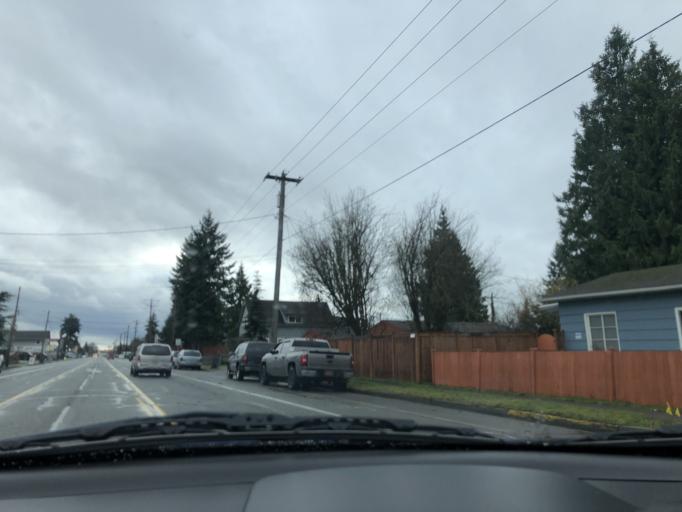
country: US
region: Washington
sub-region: Snohomish County
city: Marysville
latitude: 48.0573
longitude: -122.1804
